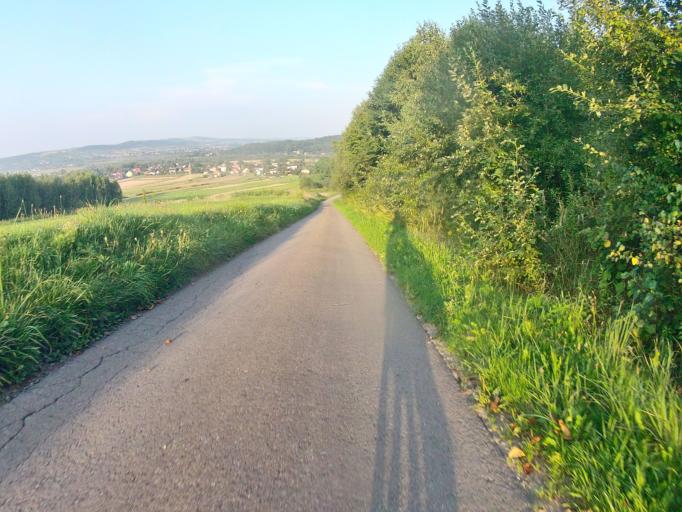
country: PL
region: Subcarpathian Voivodeship
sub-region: Powiat jasielski
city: Brzyska
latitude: 49.7864
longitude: 21.3894
